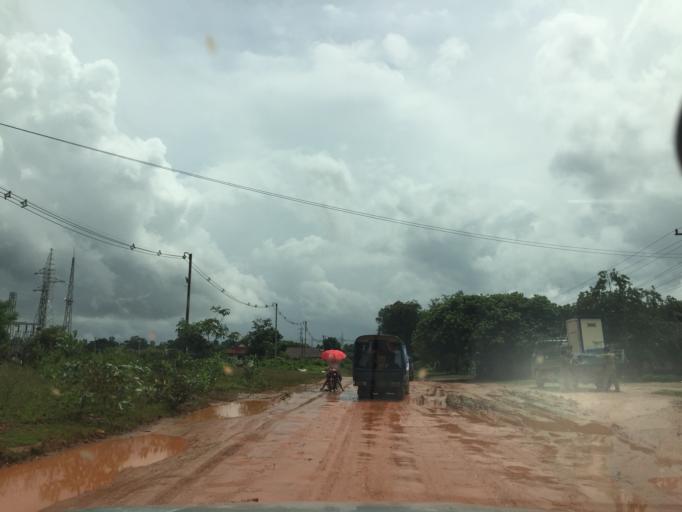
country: LA
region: Attapu
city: Attapu
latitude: 14.8132
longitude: 106.7842
